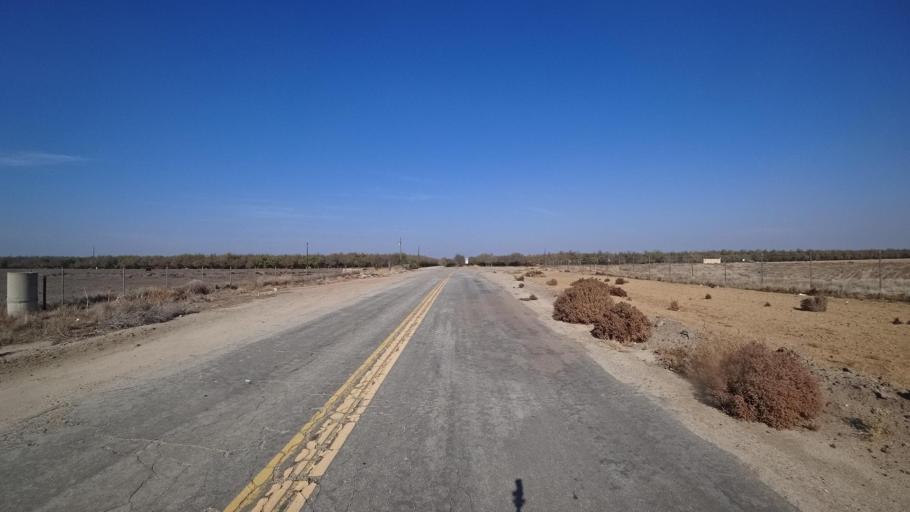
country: US
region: California
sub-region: Kern County
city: Shafter
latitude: 35.5355
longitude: -119.1868
